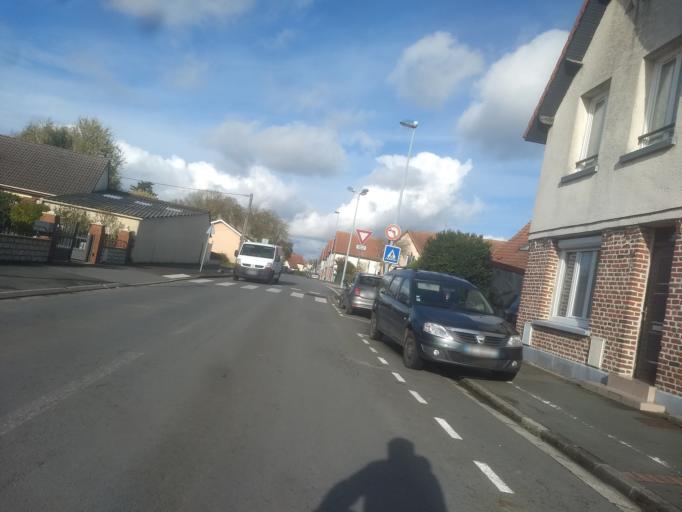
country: FR
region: Nord-Pas-de-Calais
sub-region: Departement du Pas-de-Calais
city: Beaurains
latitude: 50.2752
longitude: 2.7853
